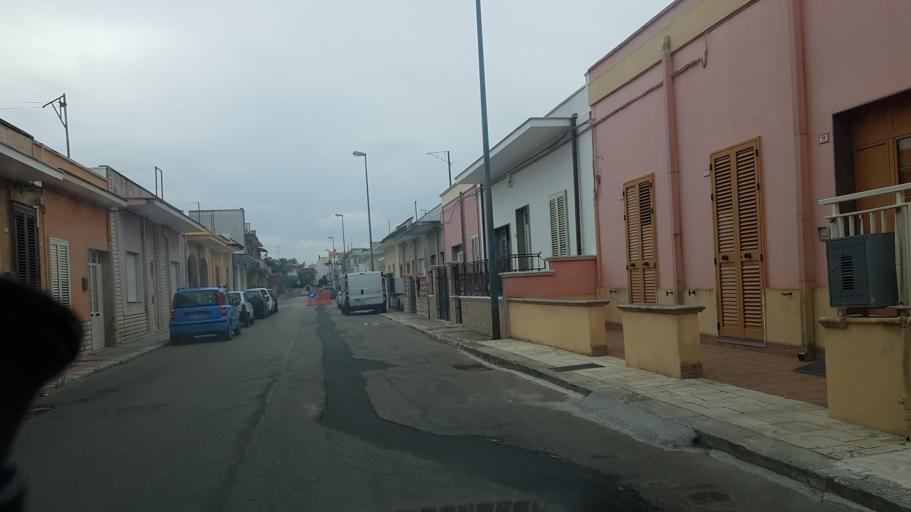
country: IT
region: Apulia
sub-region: Provincia di Brindisi
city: Cellino San Marco
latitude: 40.4706
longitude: 17.9604
